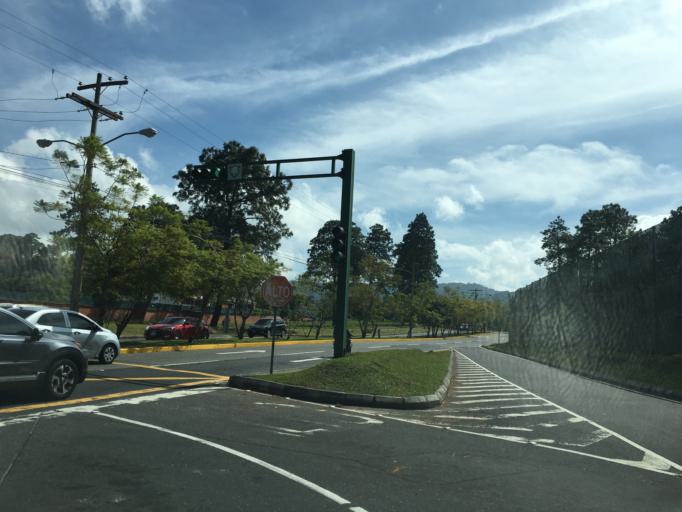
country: GT
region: Guatemala
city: Santa Catarina Pinula
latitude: 14.6034
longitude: -90.4841
